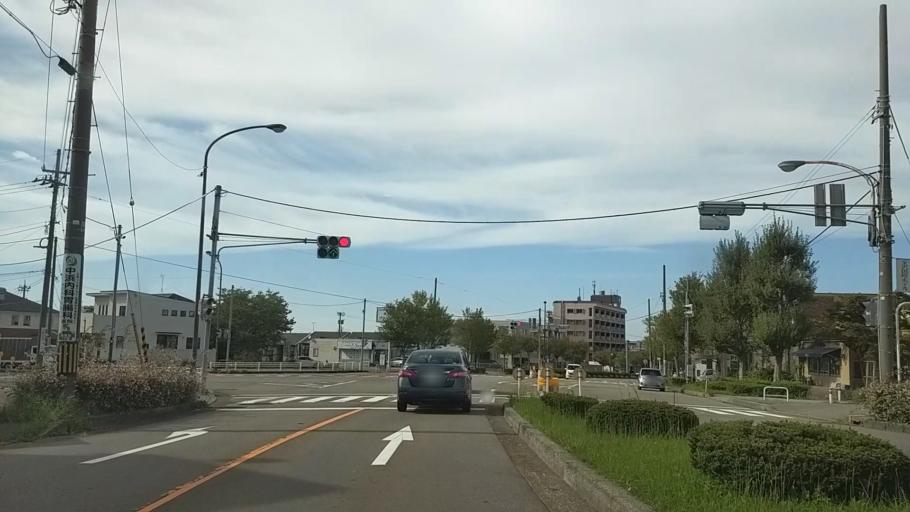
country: JP
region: Ishikawa
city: Nonoichi
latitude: 36.5237
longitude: 136.6397
